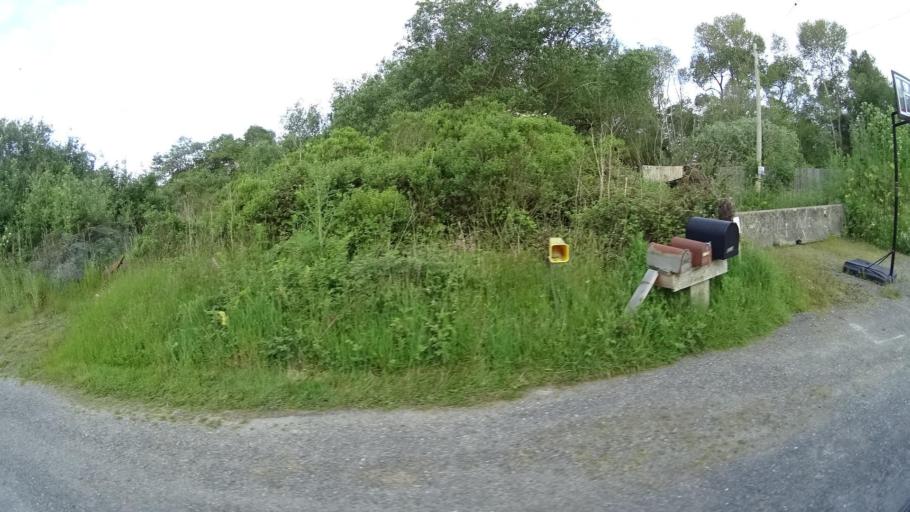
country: US
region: California
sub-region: Humboldt County
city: McKinleyville
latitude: 40.9159
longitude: -124.0912
